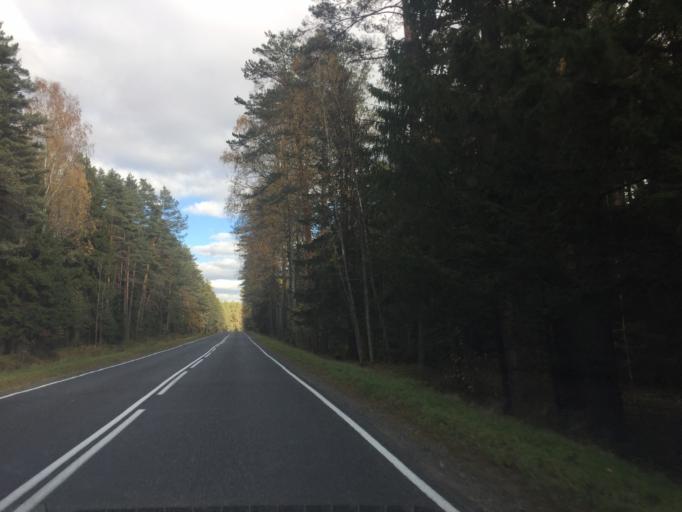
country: BY
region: Minsk
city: Narach
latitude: 54.9500
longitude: 26.5955
